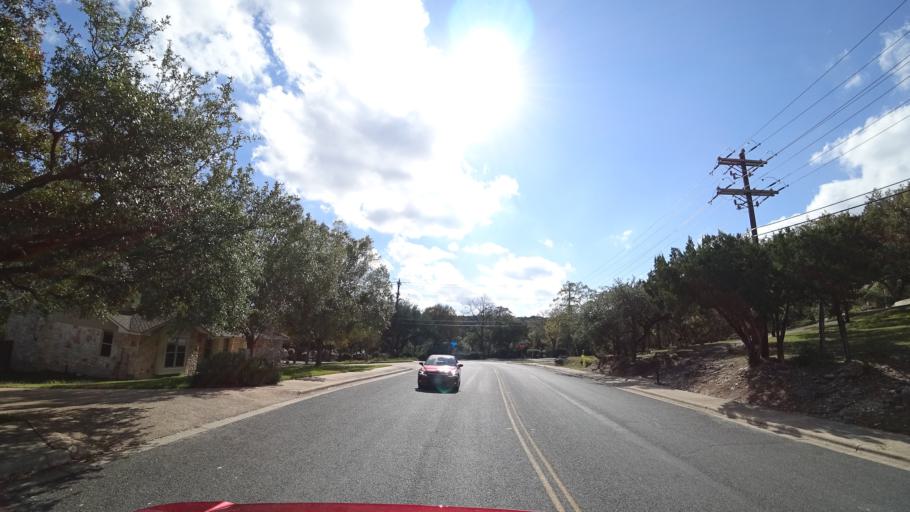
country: US
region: Texas
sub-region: Williamson County
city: Jollyville
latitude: 30.4202
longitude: -97.8015
